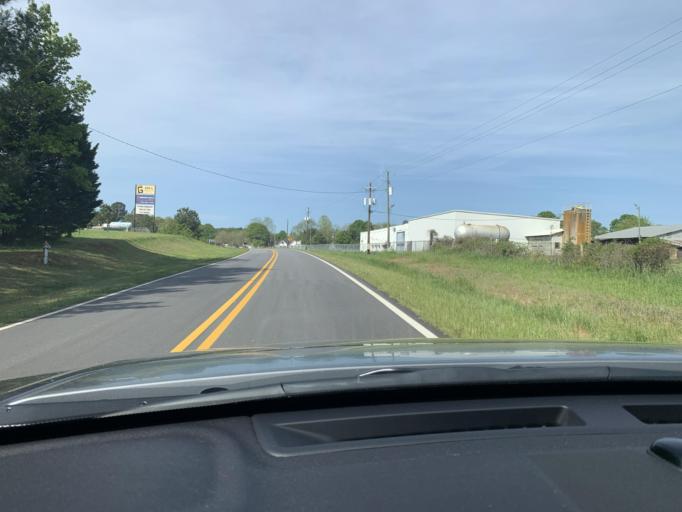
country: US
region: Georgia
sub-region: Oconee County
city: Watkinsville
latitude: 33.8168
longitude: -83.4331
